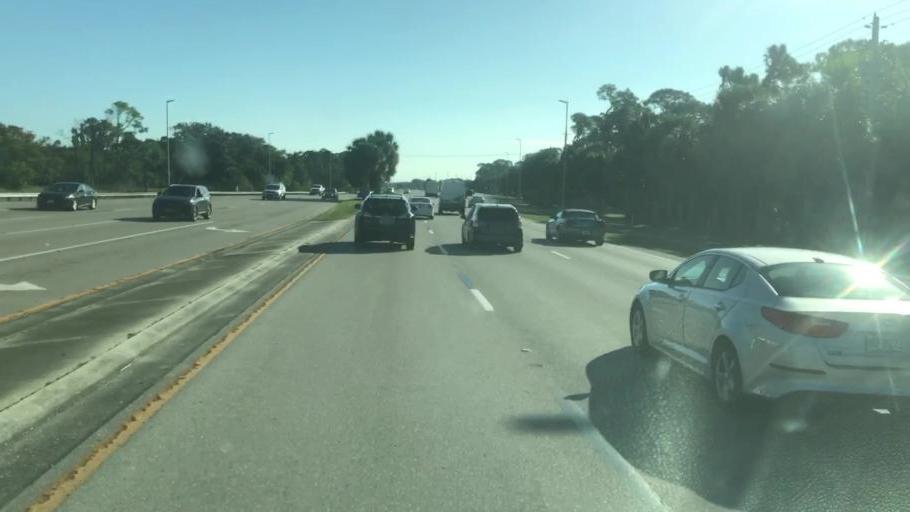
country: US
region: Florida
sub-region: Lee County
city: Villas
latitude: 26.5463
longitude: -81.8631
